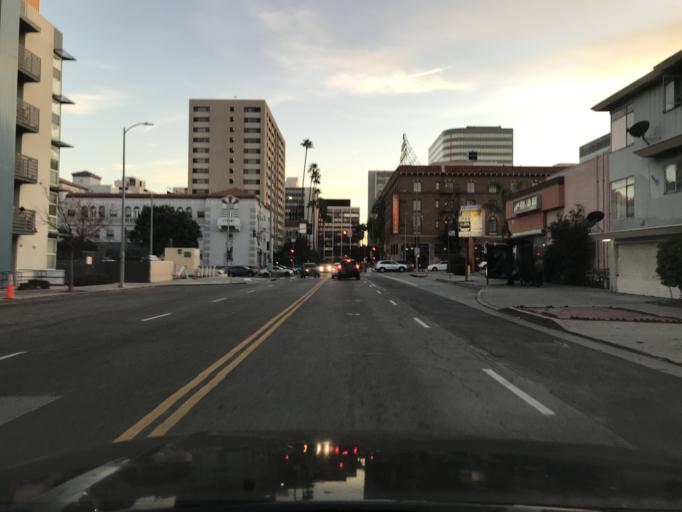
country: US
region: California
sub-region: Los Angeles County
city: Silver Lake
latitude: 34.0643
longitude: -118.3004
